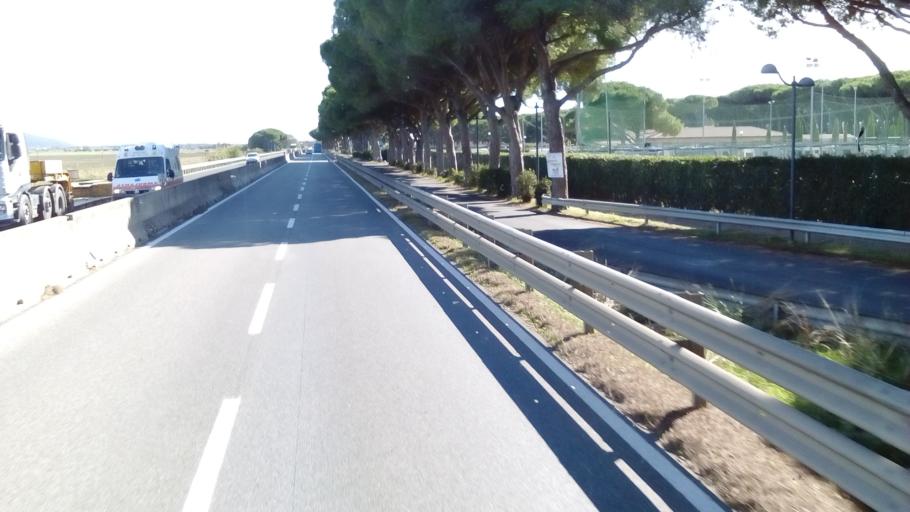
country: IT
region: Tuscany
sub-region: Provincia di Grosseto
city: Albinia
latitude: 42.5303
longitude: 11.1873
